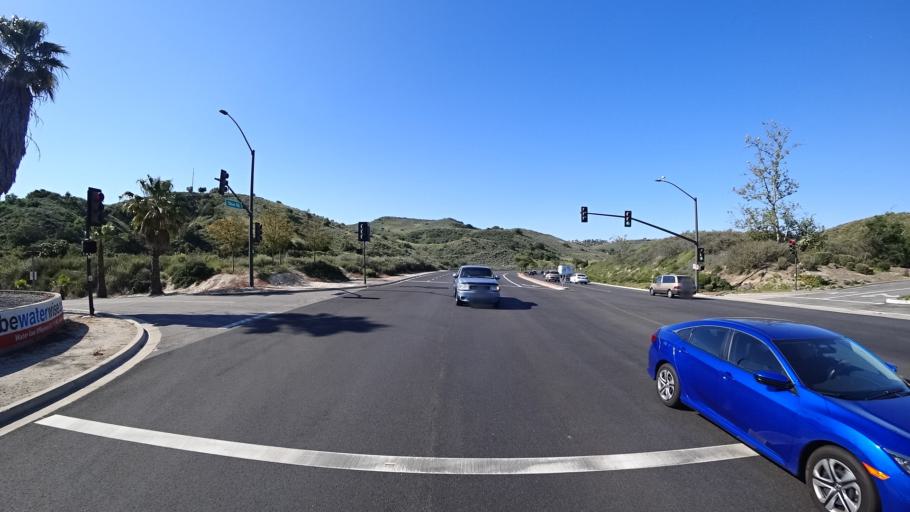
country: US
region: California
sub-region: Ventura County
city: Simi Valley
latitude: 34.2462
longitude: -118.8337
